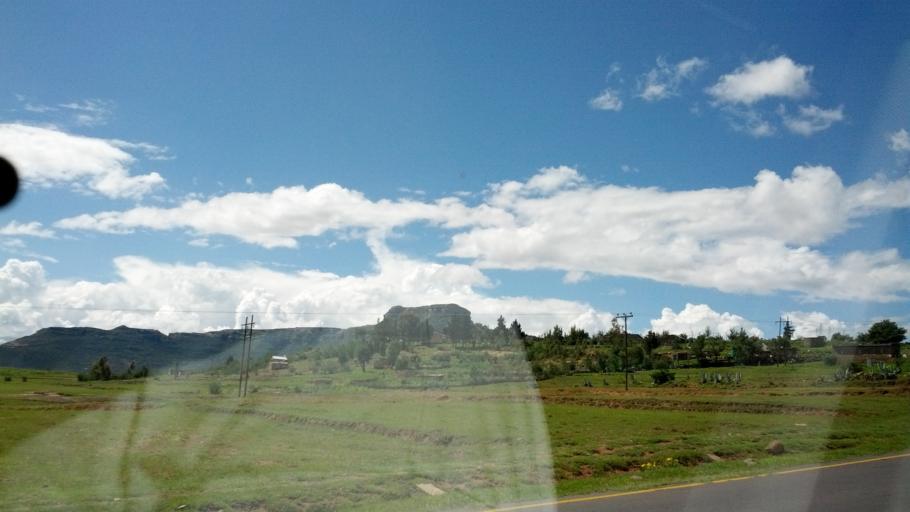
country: LS
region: Mafeteng
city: Mafeteng
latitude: -29.6478
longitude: 27.4632
